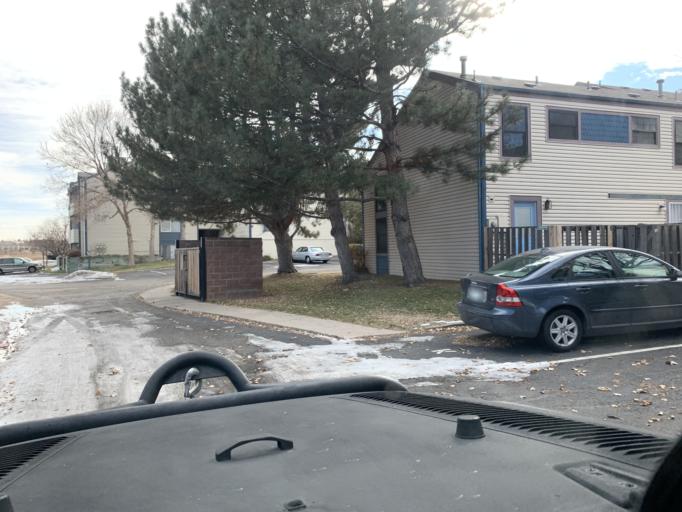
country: US
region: Colorado
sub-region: Adams County
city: Aurora
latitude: 39.7099
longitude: -104.8001
